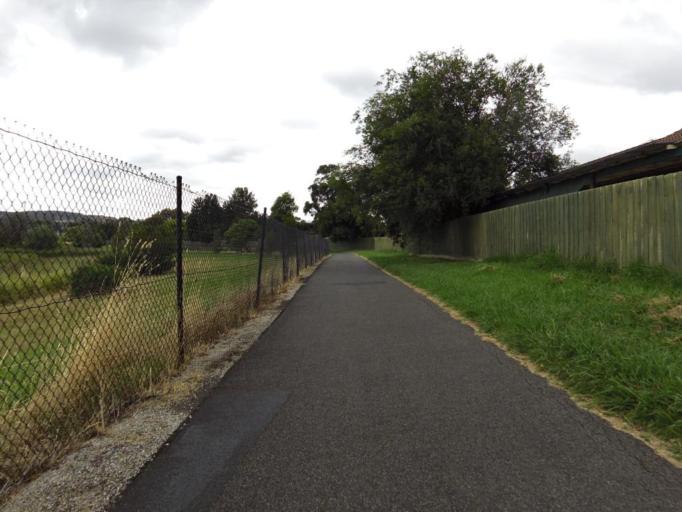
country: AU
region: Victoria
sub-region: Knox
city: Knoxfield
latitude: -37.9106
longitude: 145.2537
